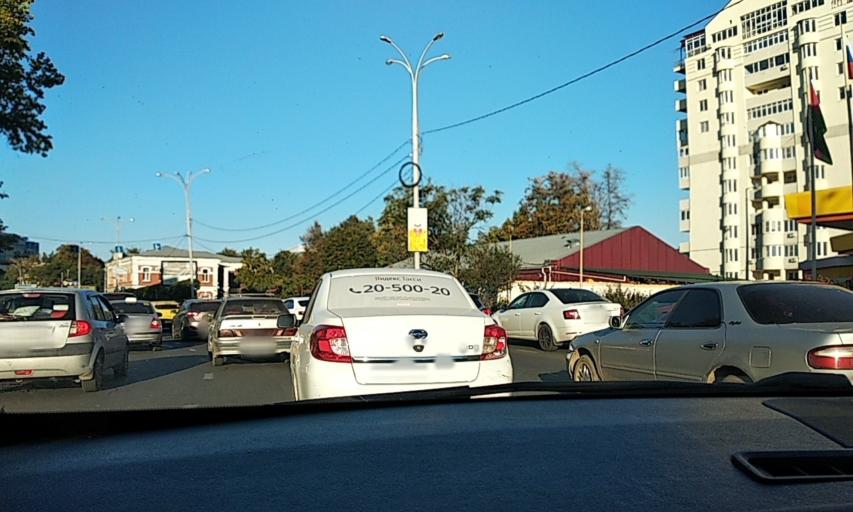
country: RU
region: Krasnodarskiy
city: Krasnodar
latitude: 45.0249
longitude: 38.9933
